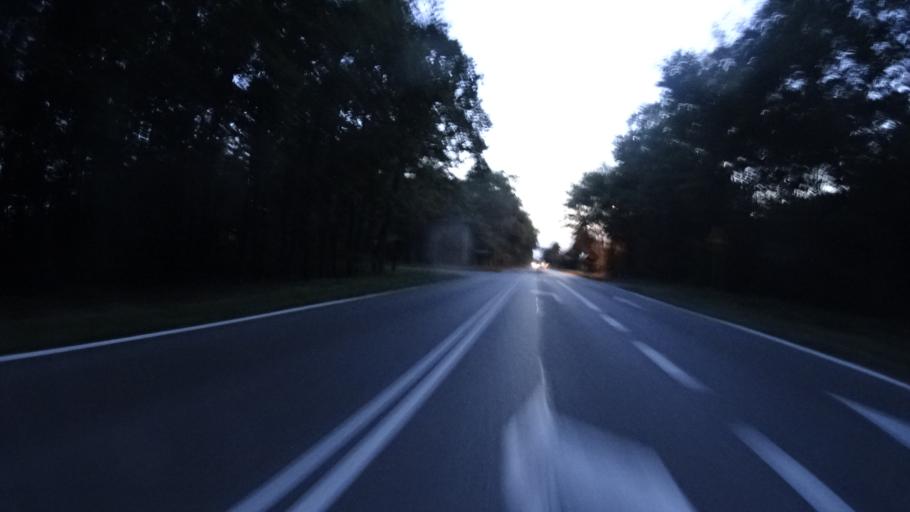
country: PL
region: Masovian Voivodeship
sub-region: Powiat warszawski zachodni
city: Leszno
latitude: 52.2631
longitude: 20.6535
